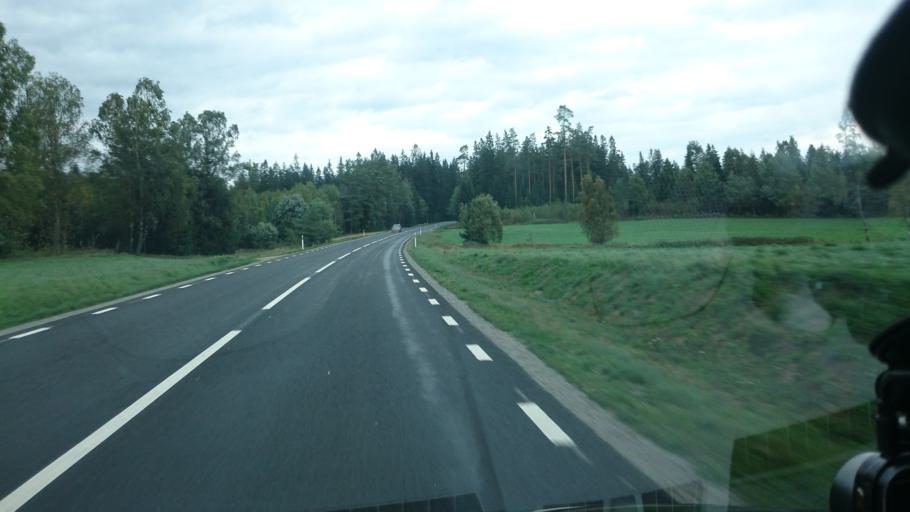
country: SE
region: Vaestra Goetaland
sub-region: Svenljunga Kommun
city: Svenljunga
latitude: 57.5534
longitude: 13.1211
